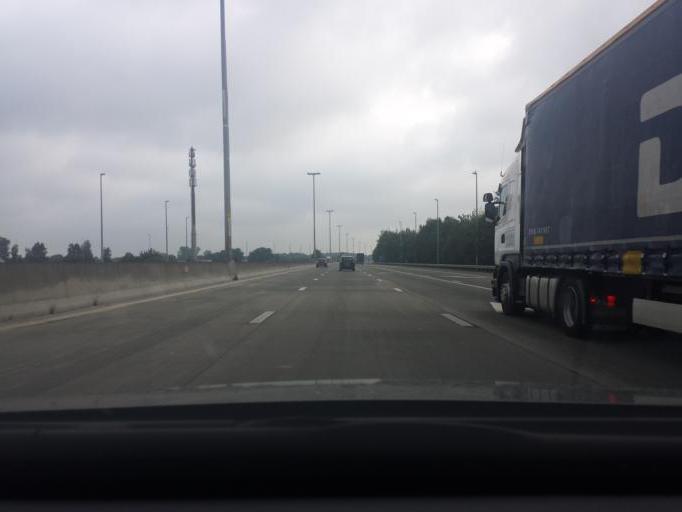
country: BE
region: Flanders
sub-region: Provincie Oost-Vlaanderen
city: Nazareth
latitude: 50.9559
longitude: 3.5645
